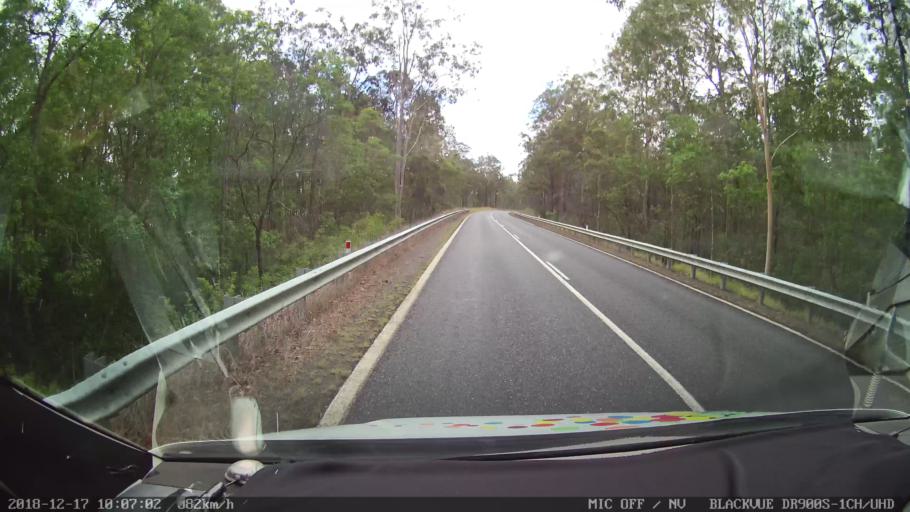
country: AU
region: New South Wales
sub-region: Tenterfield Municipality
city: Carrolls Creek
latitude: -28.8894
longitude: 152.5126
